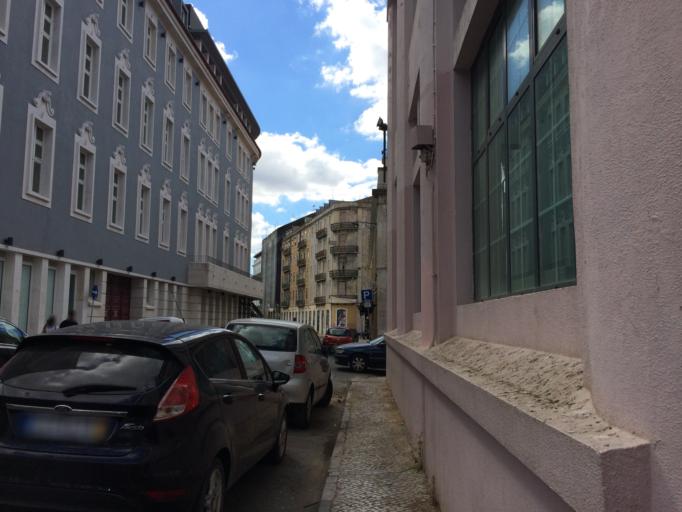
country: PT
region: Lisbon
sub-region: Lisbon
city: Lisbon
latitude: 38.7083
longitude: -9.1469
